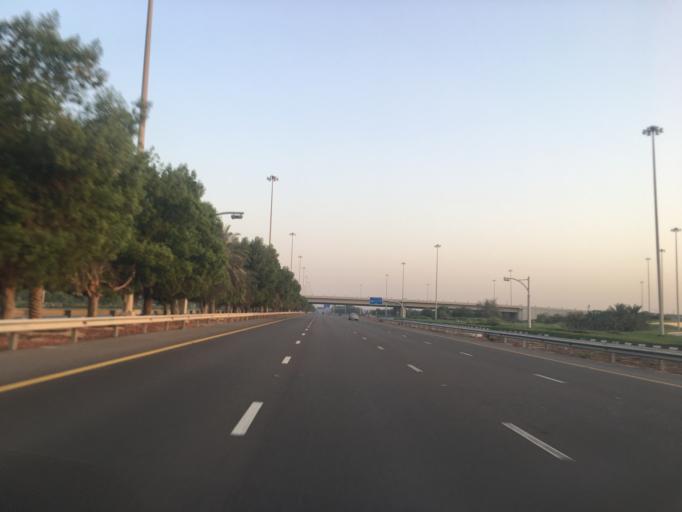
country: AE
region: Abu Dhabi
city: Abu Dhabi
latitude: 24.3730
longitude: 54.5544
